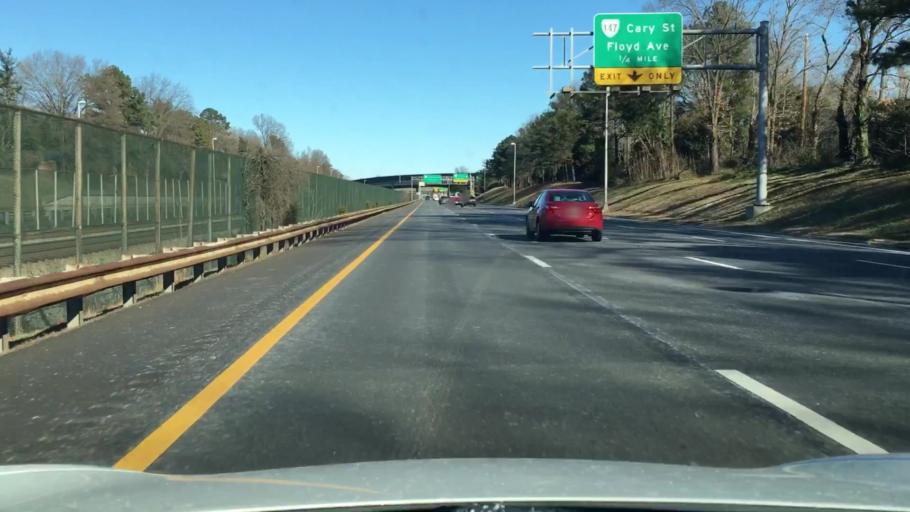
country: US
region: Virginia
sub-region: City of Richmond
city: Richmond
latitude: 37.5498
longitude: -77.4911
